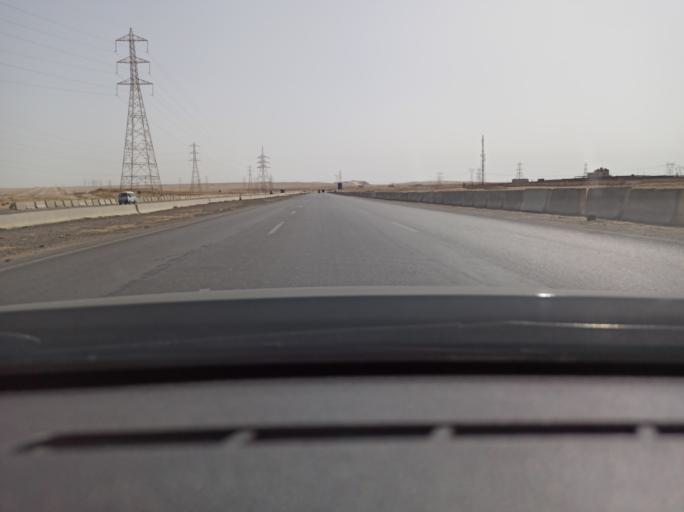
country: EG
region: Muhafazat al Qahirah
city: Halwan
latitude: 29.7669
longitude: 31.3896
